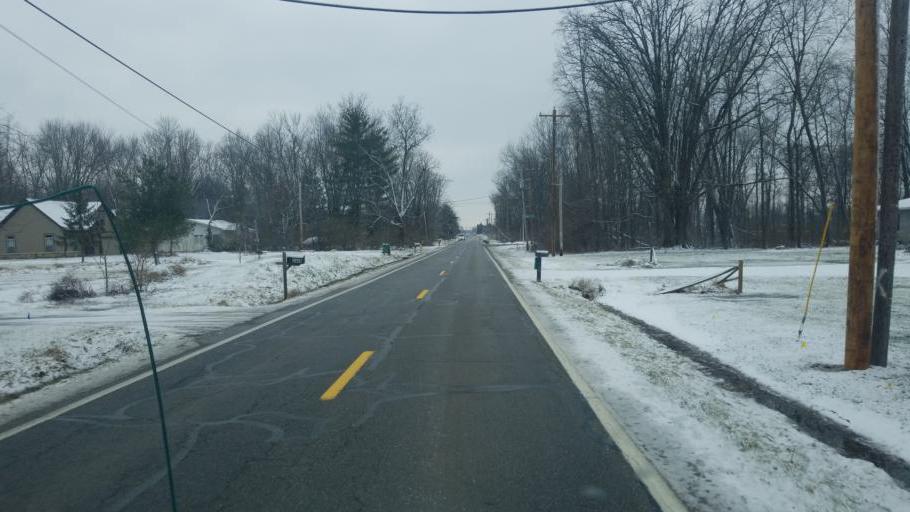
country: US
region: Ohio
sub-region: Franklin County
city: New Albany
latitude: 40.0244
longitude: -82.7892
